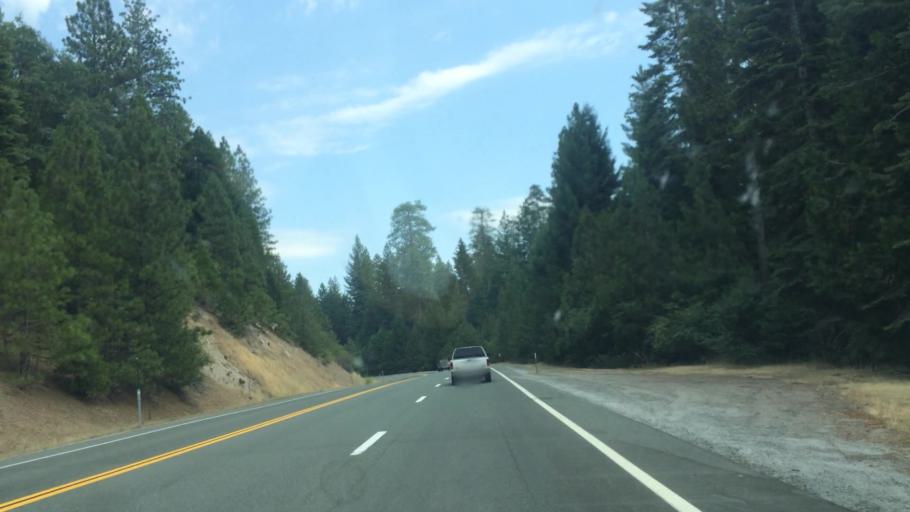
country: US
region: California
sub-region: Amador County
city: Pioneer
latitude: 38.5145
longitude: -120.4677
